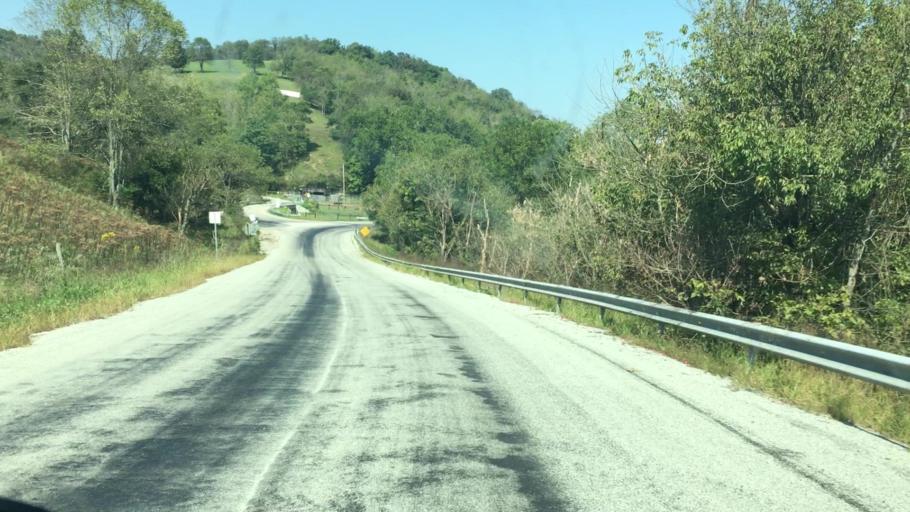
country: US
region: Pennsylvania
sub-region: Greene County
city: Waynesburg
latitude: 39.9393
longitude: -80.2884
